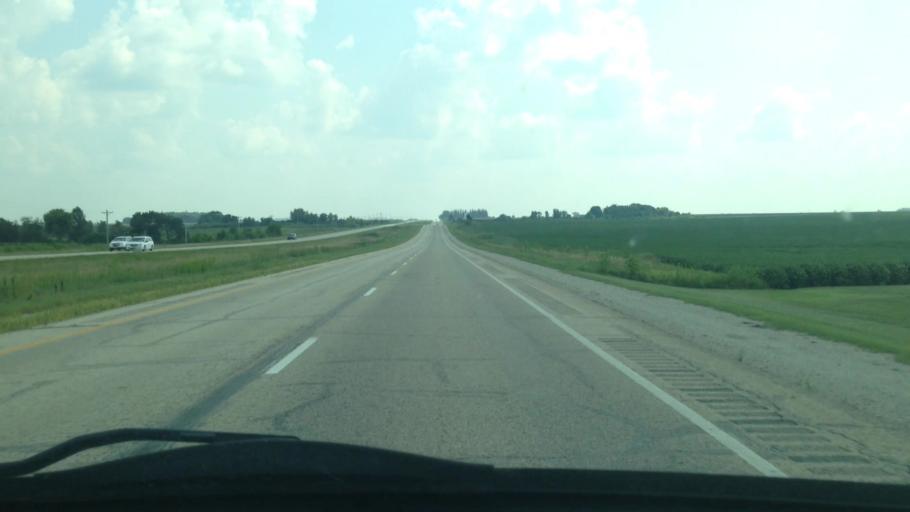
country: US
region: Iowa
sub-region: Bremer County
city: Tripoli
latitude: 42.8727
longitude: -92.3378
